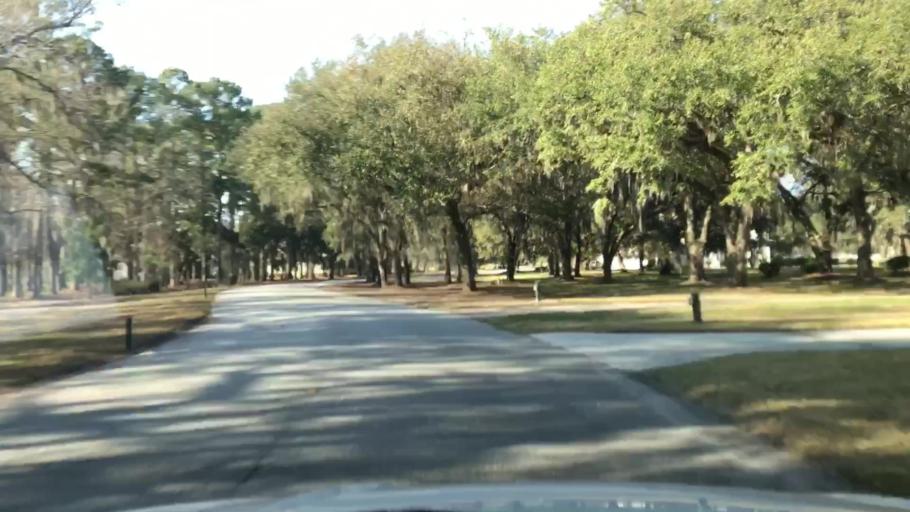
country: US
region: South Carolina
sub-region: Beaufort County
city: Bluffton
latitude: 32.3379
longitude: -80.9103
